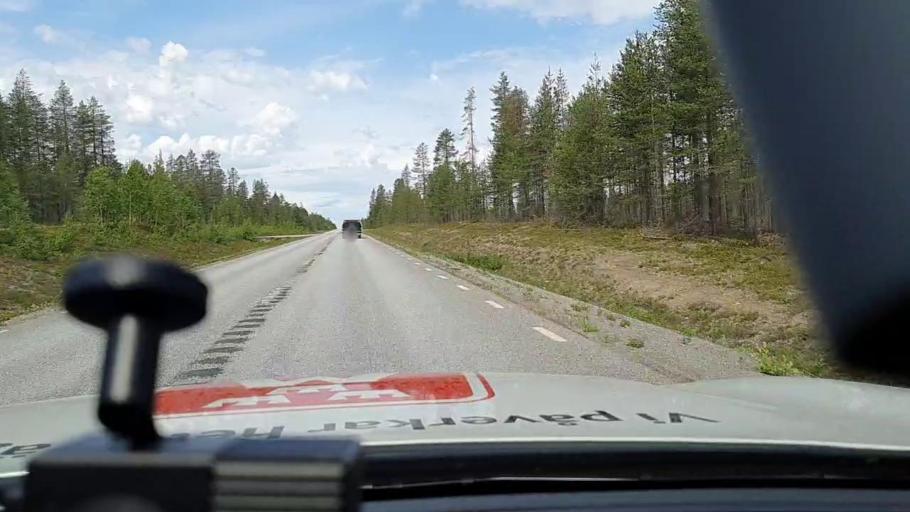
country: SE
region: Norrbotten
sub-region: Jokkmokks Kommun
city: Jokkmokk
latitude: 66.5231
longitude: 20.2054
